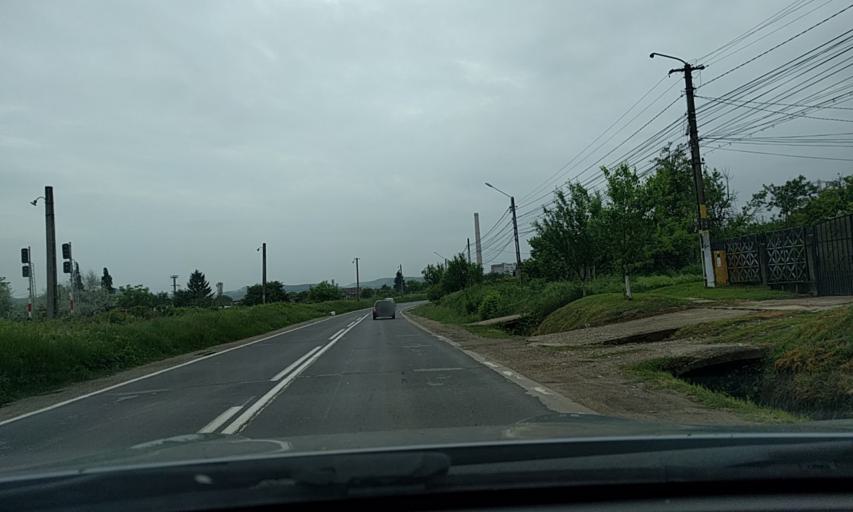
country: RO
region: Dambovita
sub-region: Comuna Doicesti
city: Doicesti
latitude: 44.9895
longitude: 25.4096
